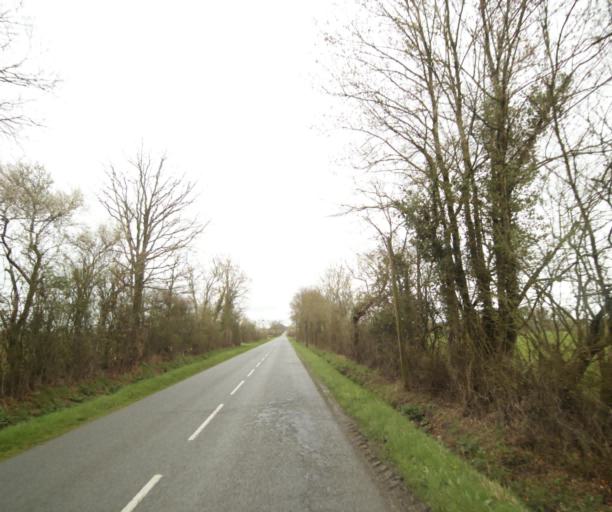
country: FR
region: Pays de la Loire
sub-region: Departement de la Loire-Atlantique
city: Bouvron
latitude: 47.4490
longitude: -1.8646
